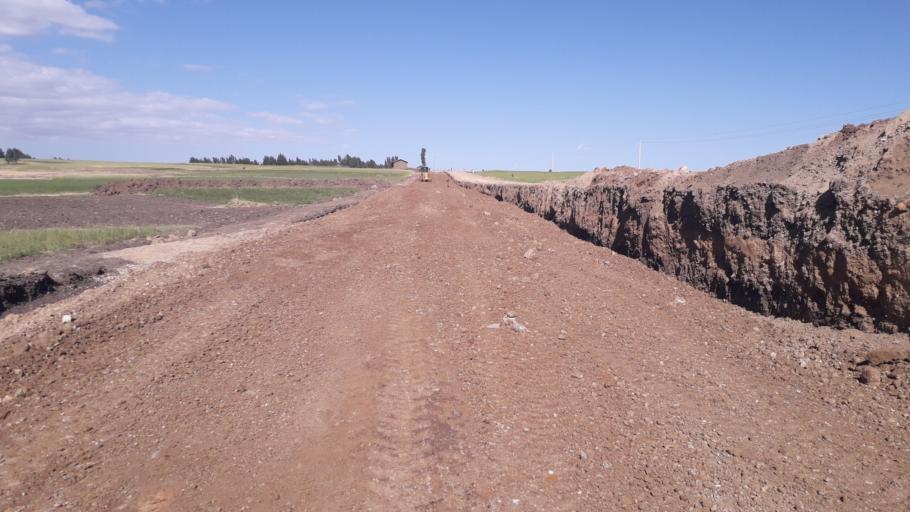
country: ET
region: Amhara
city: Lalibela
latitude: 11.5582
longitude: 39.1237
